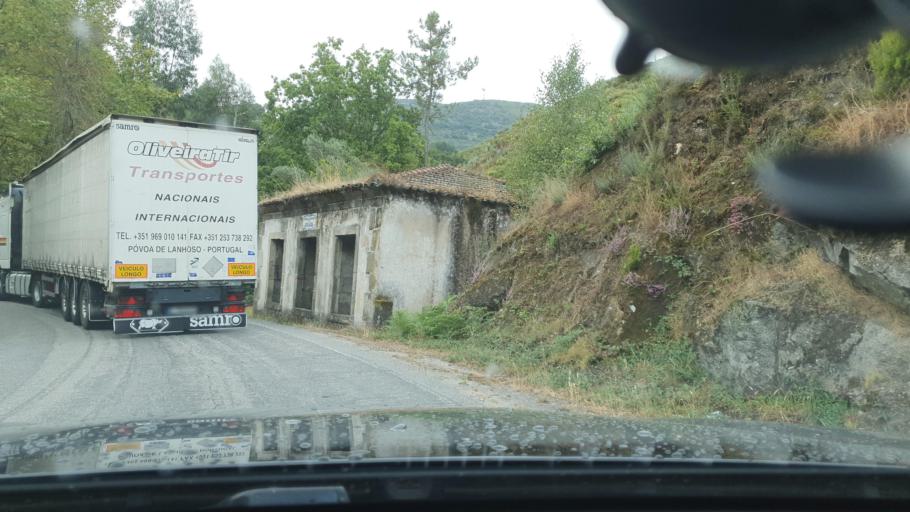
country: PT
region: Braga
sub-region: Vieira do Minho
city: Vieira do Minho
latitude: 41.6745
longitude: -8.0591
